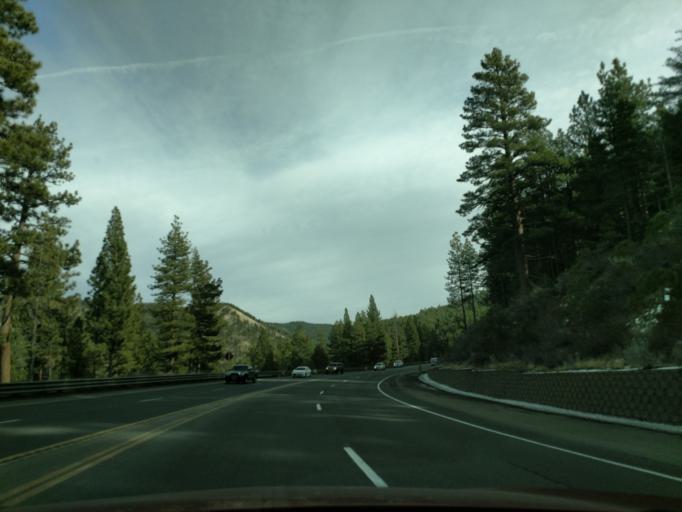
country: US
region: Nevada
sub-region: Douglas County
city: Kingsbury
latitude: 39.0823
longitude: -119.9410
